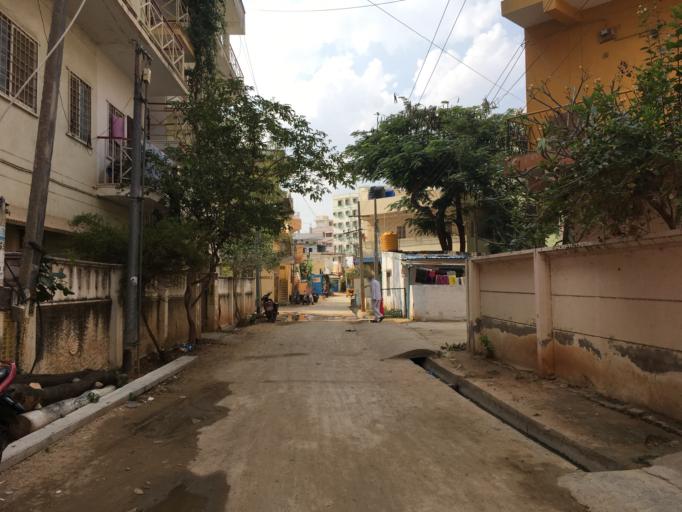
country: IN
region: Andhra Pradesh
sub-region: Anantapur
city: Puttaparthi
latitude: 14.1679
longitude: 77.8130
